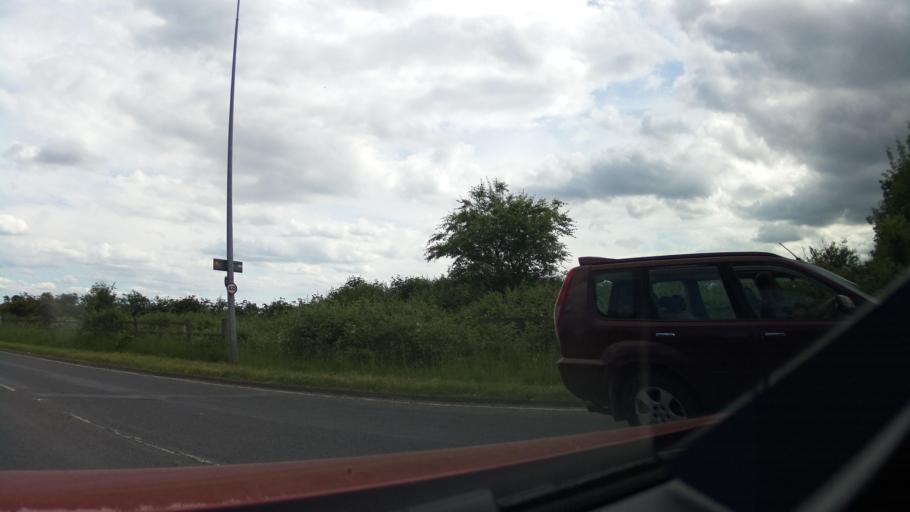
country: GB
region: England
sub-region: Worcestershire
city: Worcester
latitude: 52.1678
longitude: -2.1789
